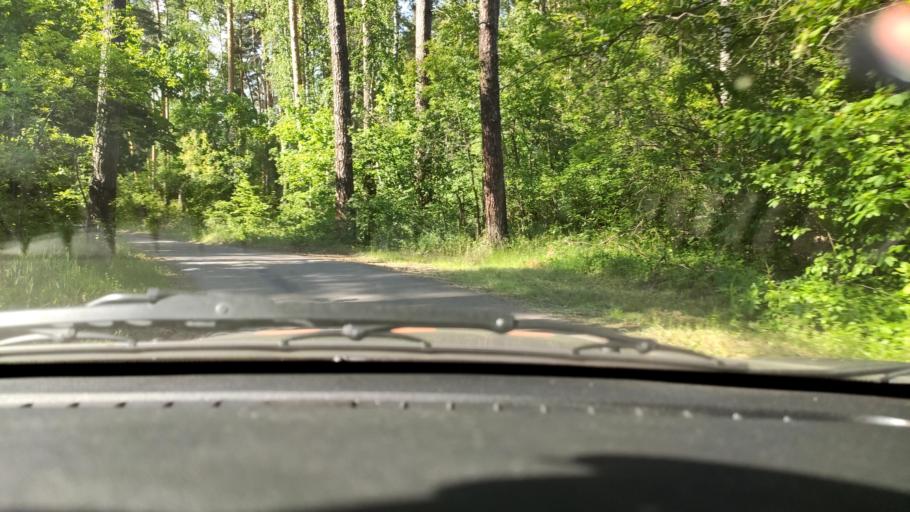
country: RU
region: Voronezj
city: Somovo
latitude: 51.8016
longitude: 39.3806
